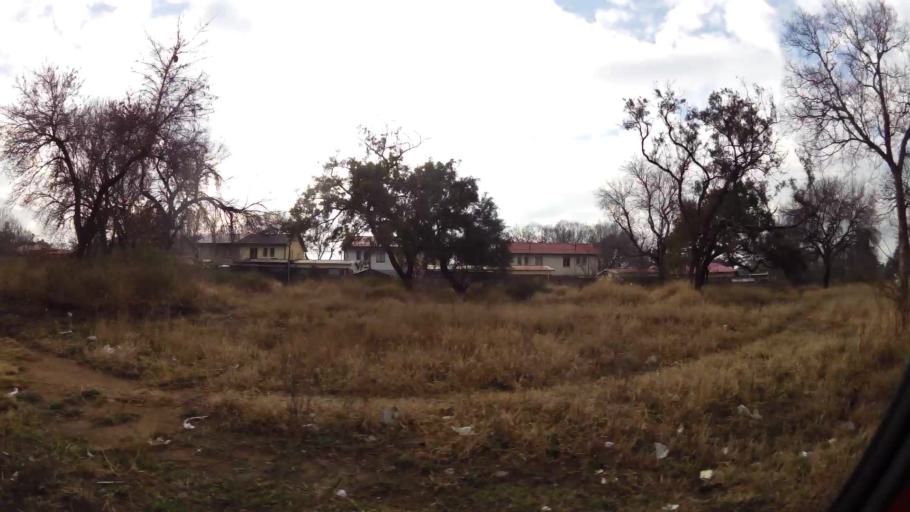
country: ZA
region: Gauteng
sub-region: Sedibeng District Municipality
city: Vanderbijlpark
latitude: -26.6967
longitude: 27.8120
